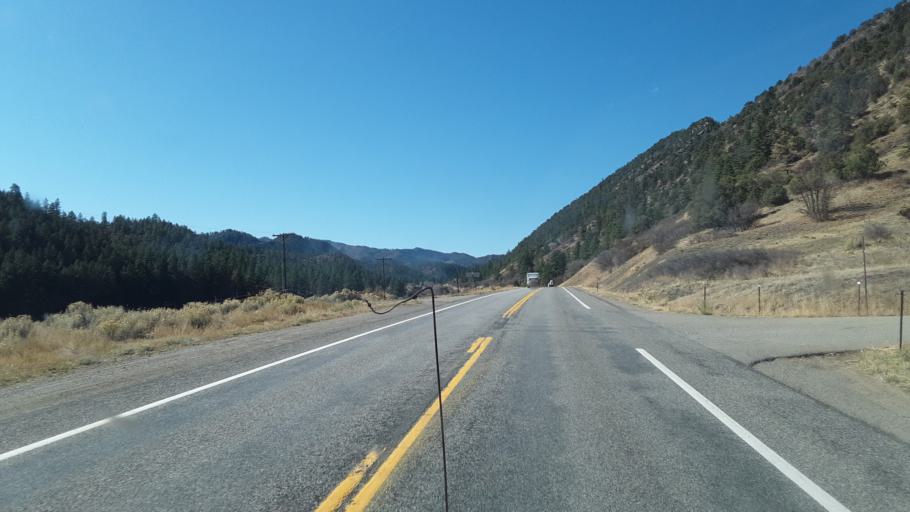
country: US
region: Colorado
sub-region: La Plata County
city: Bayfield
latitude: 37.2289
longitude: -107.3576
